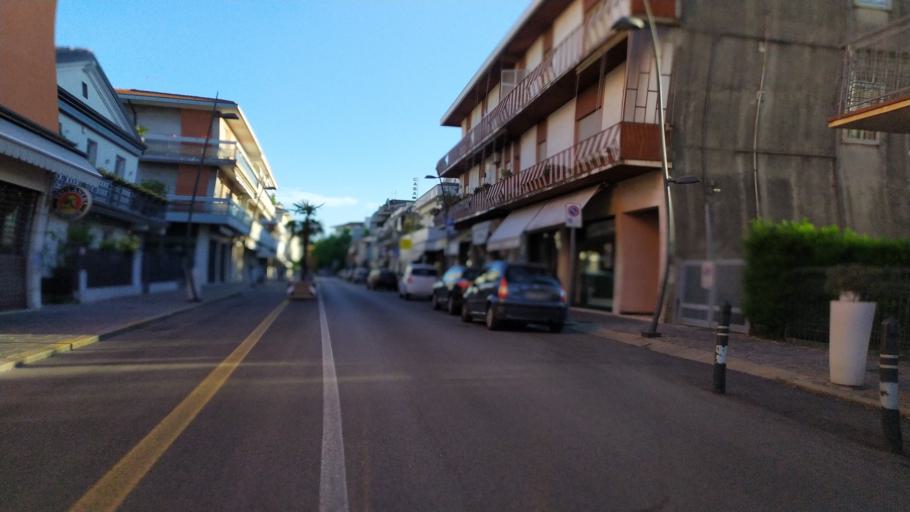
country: IT
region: Veneto
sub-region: Provincia di Padova
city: Abano Terme
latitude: 45.3510
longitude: 11.7879
